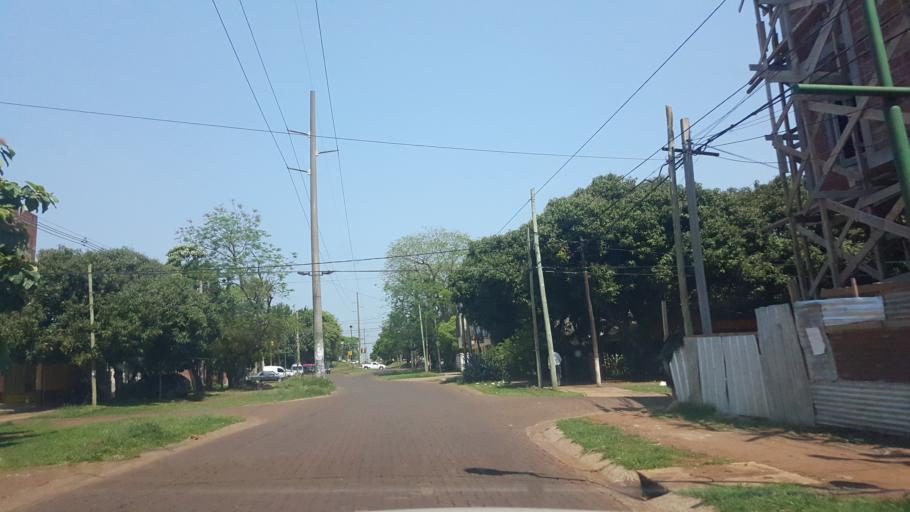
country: AR
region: Misiones
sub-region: Departamento de Capital
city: Posadas
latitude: -27.3848
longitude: -55.9152
